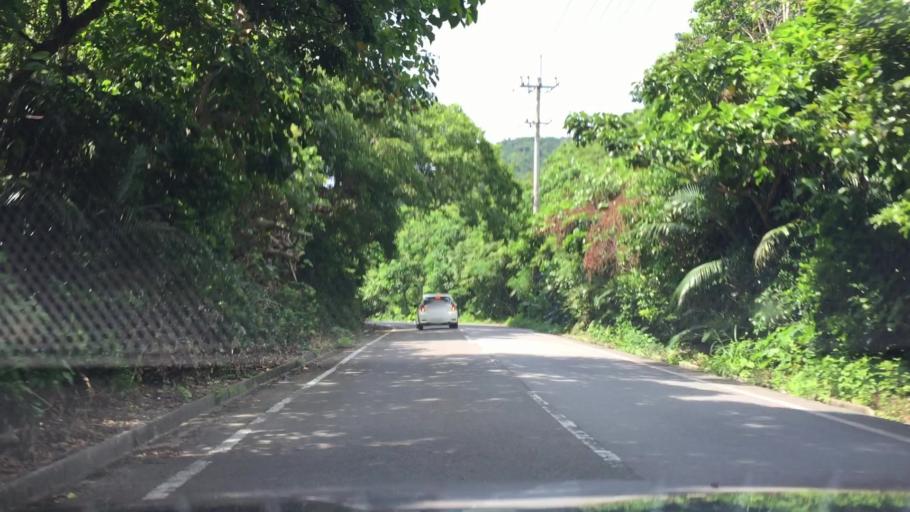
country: JP
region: Okinawa
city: Ishigaki
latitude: 24.4644
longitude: 124.2268
